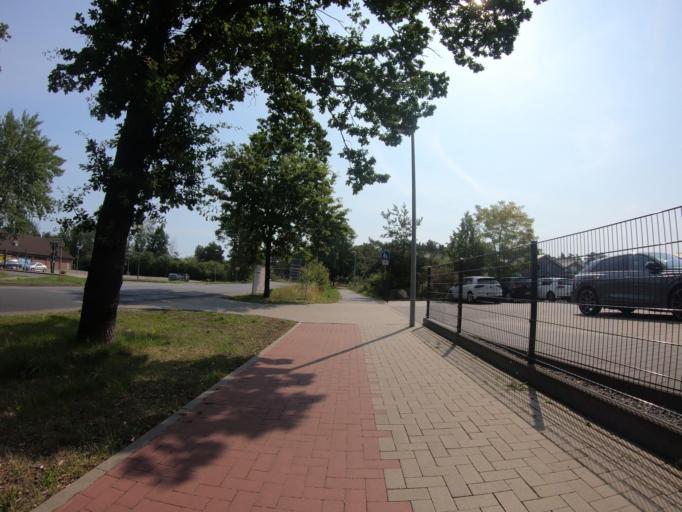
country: DE
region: Lower Saxony
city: Gifhorn
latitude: 52.4676
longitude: 10.5749
